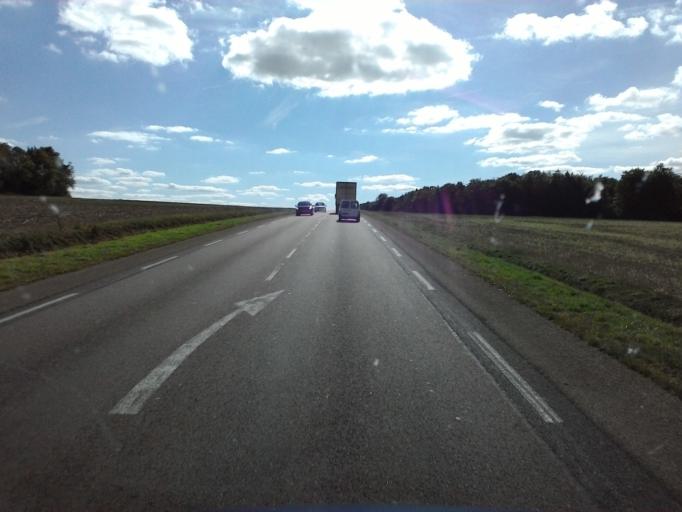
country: FR
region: Bourgogne
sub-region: Departement de la Cote-d'Or
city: Chatillon-sur-Seine
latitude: 47.7871
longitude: 4.5127
